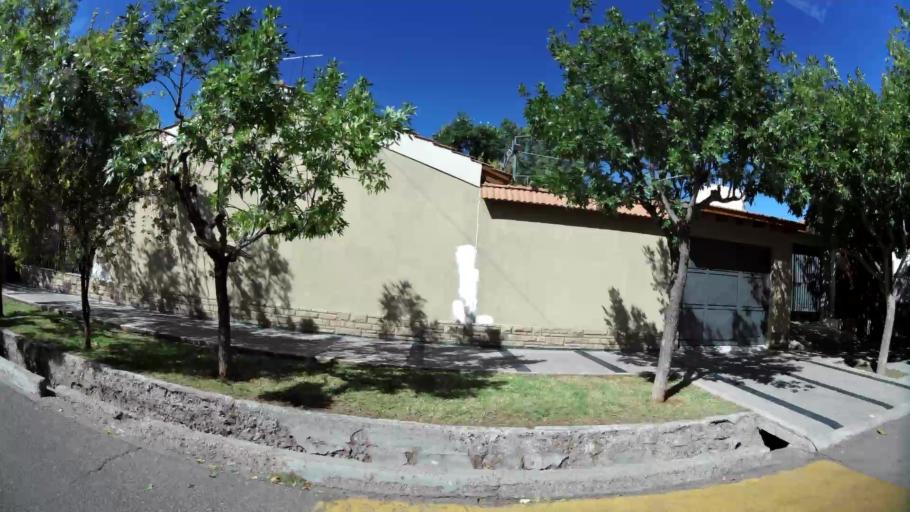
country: AR
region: Mendoza
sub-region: Departamento de Maipu
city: Maipu
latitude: -32.9723
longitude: -68.7978
